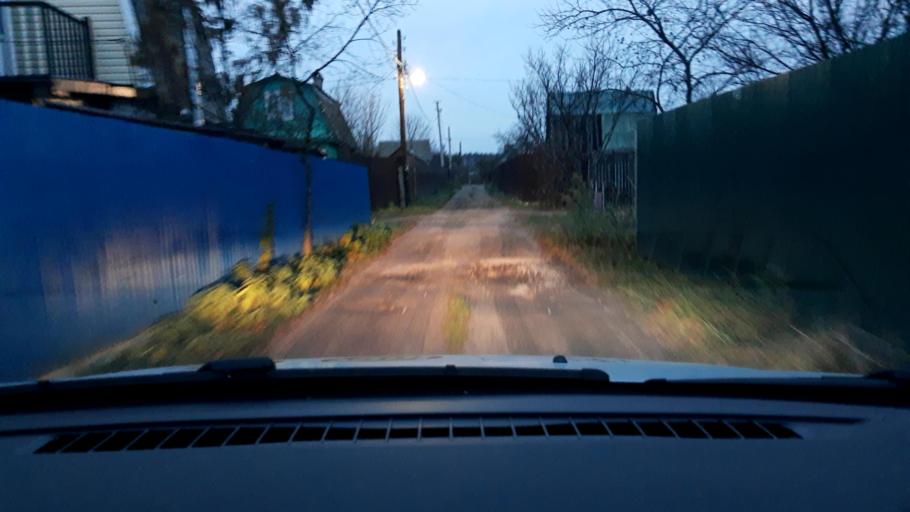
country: RU
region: Nizjnij Novgorod
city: Neklyudovo
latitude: 56.4287
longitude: 44.0095
